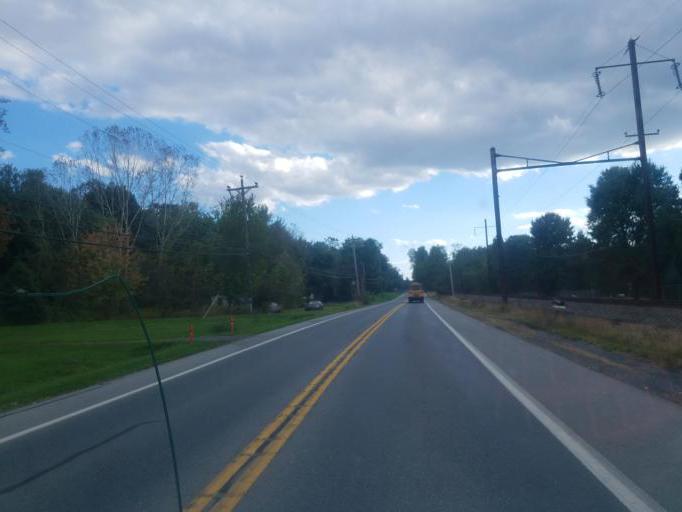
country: US
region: Pennsylvania
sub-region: Dauphin County
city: Middletown
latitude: 40.1768
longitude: -76.7240
